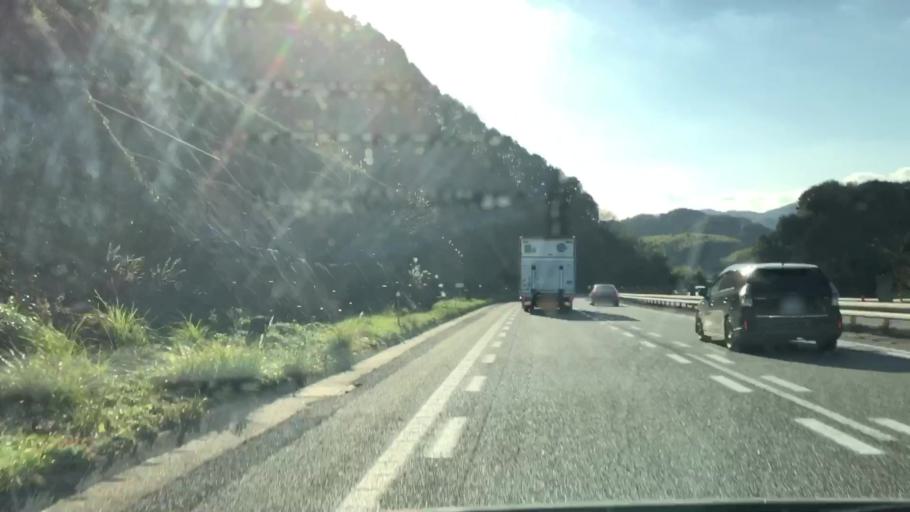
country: JP
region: Yamaguchi
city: Onoda
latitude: 34.1109
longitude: 131.1568
